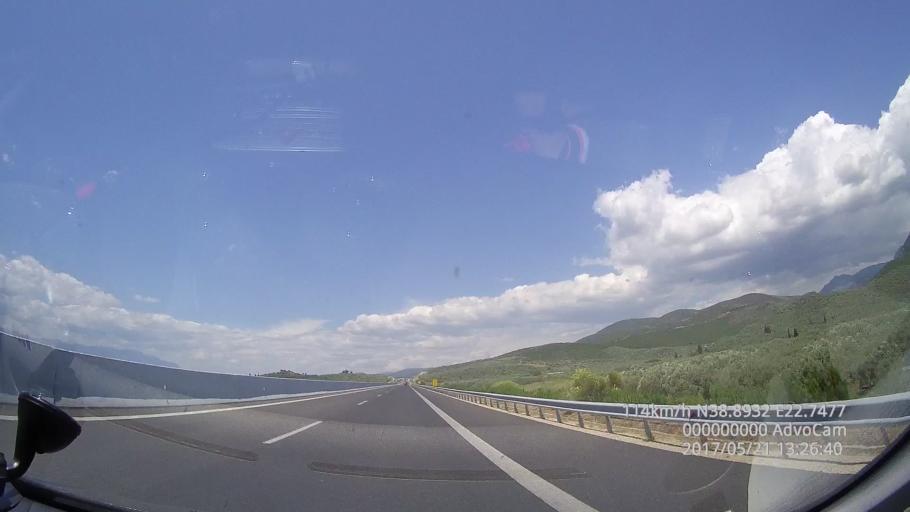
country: GR
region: Central Greece
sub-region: Nomos Fthiotidos
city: Kainouryion
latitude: 38.8934
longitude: 22.7472
